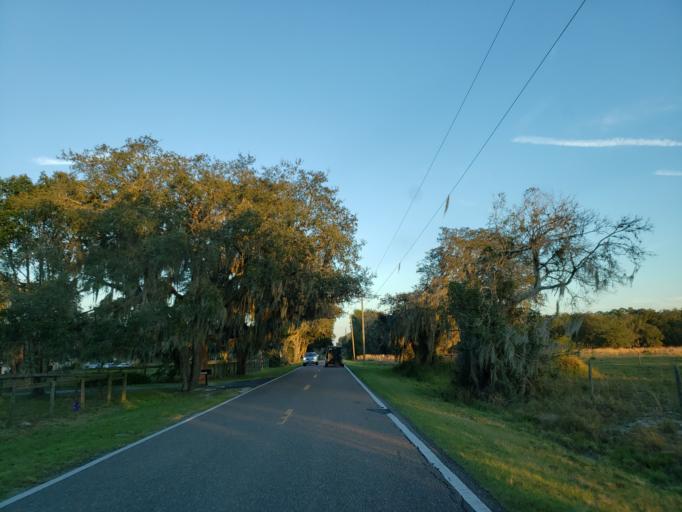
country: US
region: Florida
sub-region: Hillsborough County
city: Fish Hawk
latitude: 27.8286
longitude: -82.1927
